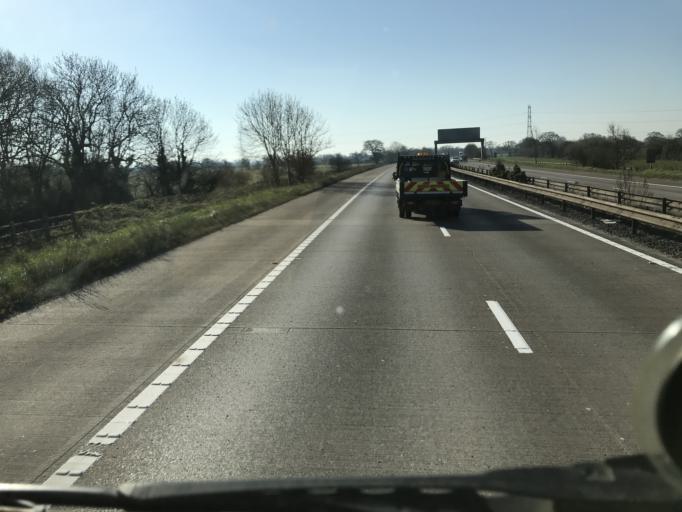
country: GB
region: England
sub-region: Cheshire West and Chester
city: Stoke
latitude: 53.2387
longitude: -2.8623
